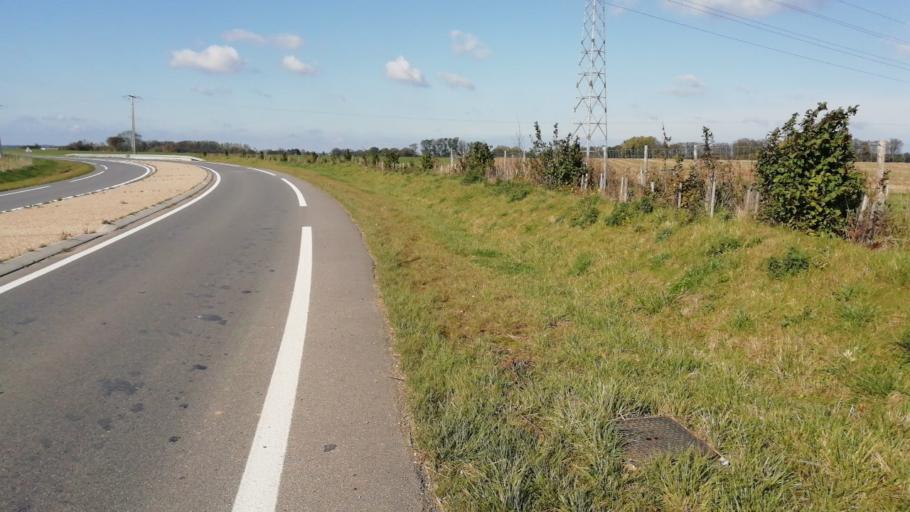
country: FR
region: Haute-Normandie
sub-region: Departement de la Seine-Maritime
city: Maneglise
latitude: 49.5907
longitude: 0.2733
